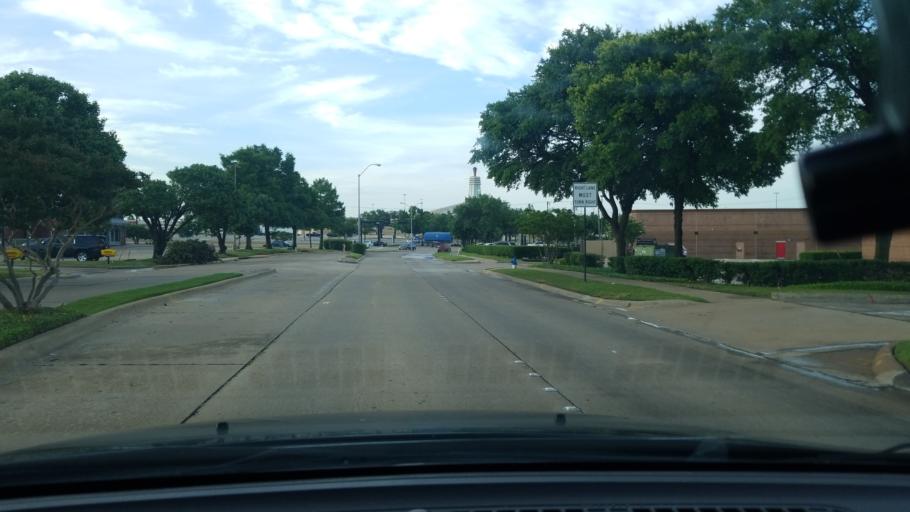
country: US
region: Texas
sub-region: Dallas County
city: Mesquite
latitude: 32.8119
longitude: -96.6255
